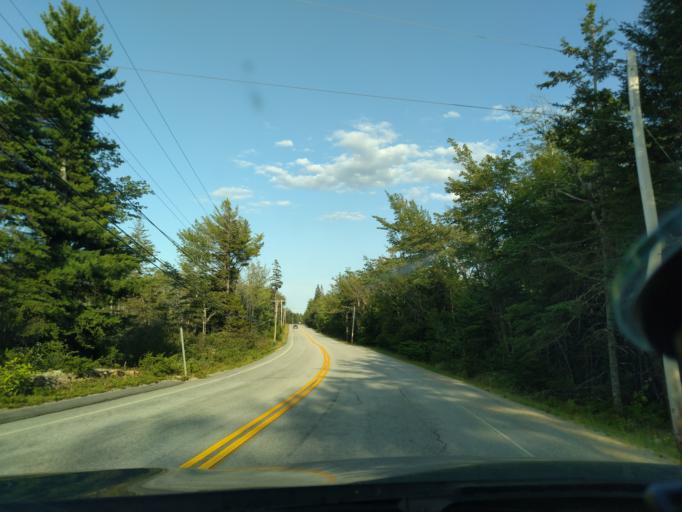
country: US
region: Maine
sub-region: Hancock County
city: Gouldsboro
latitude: 44.3935
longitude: -68.0636
